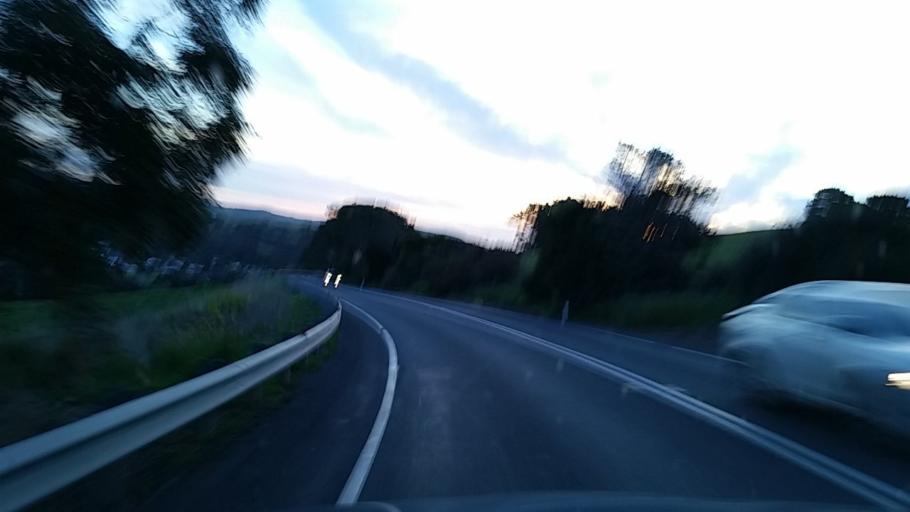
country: AU
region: South Australia
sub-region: Yankalilla
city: Normanville
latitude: -35.4552
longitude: 138.3613
